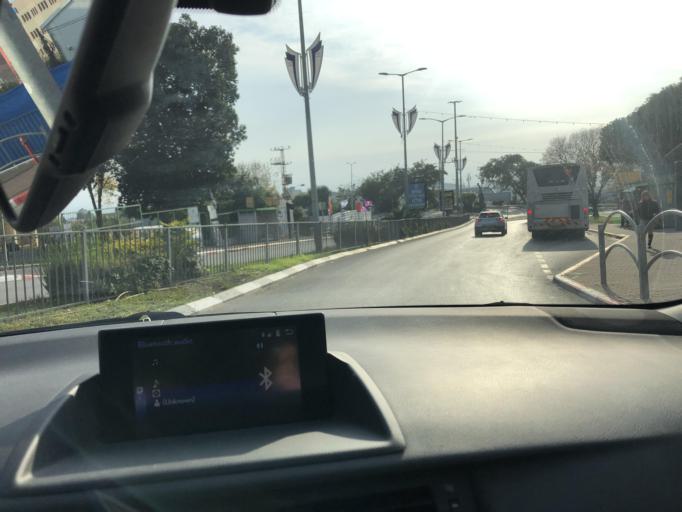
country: IL
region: Northern District
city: Nazareth
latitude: 32.7018
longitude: 35.3131
